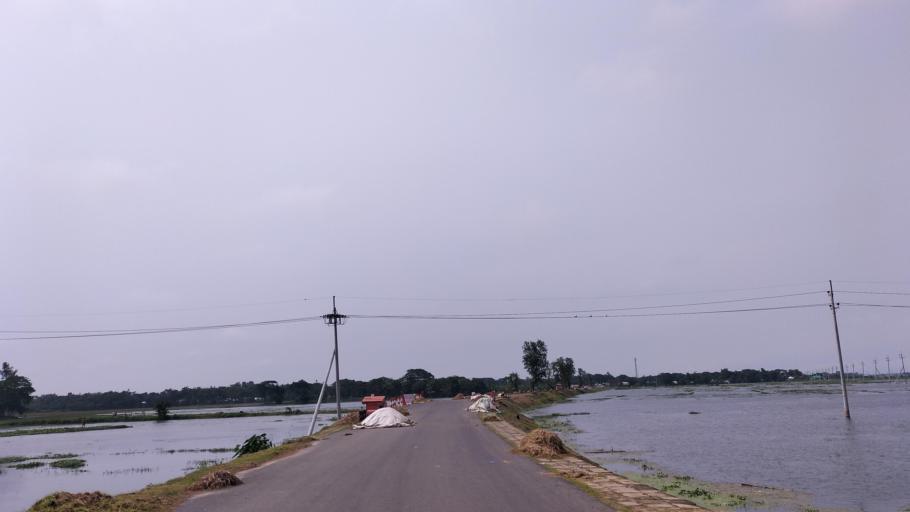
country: BD
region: Dhaka
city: Netrakona
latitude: 24.9608
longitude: 90.8338
